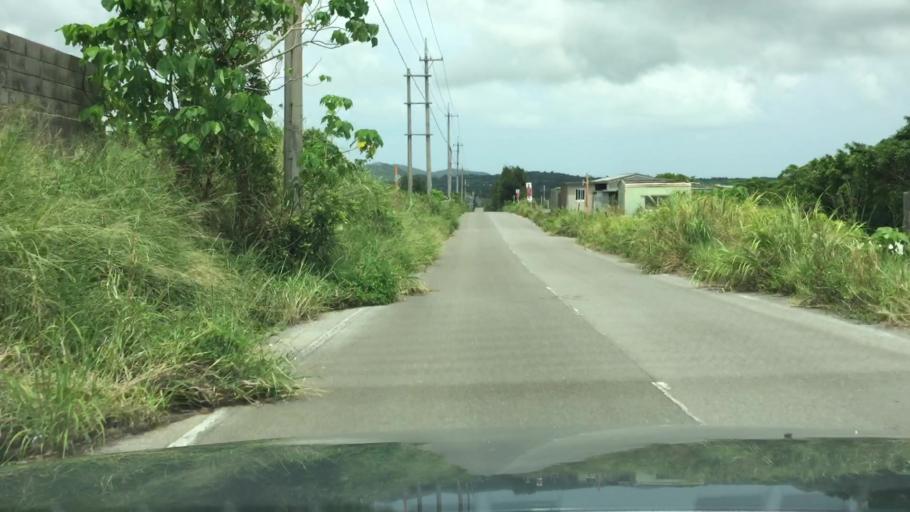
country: JP
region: Okinawa
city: Ishigaki
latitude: 24.3960
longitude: 124.1825
